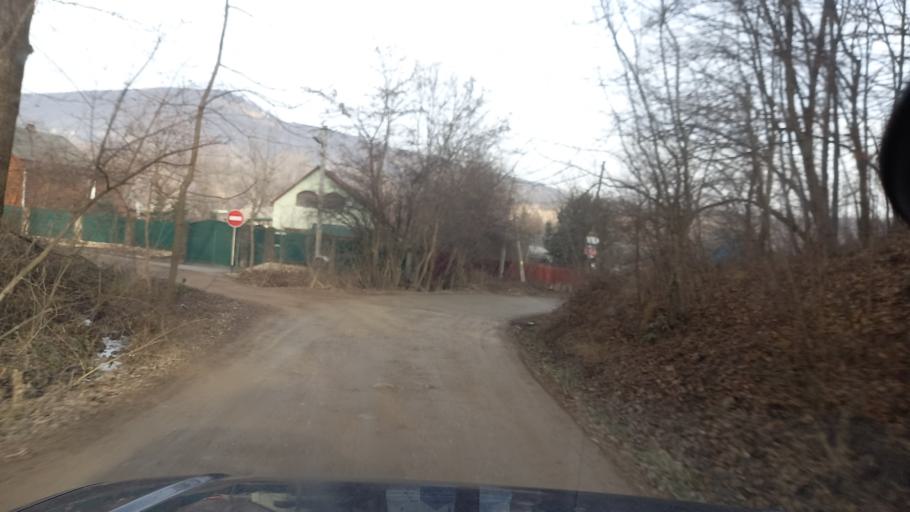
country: RU
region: Adygeya
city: Kamennomostskiy
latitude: 44.2985
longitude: 40.1794
